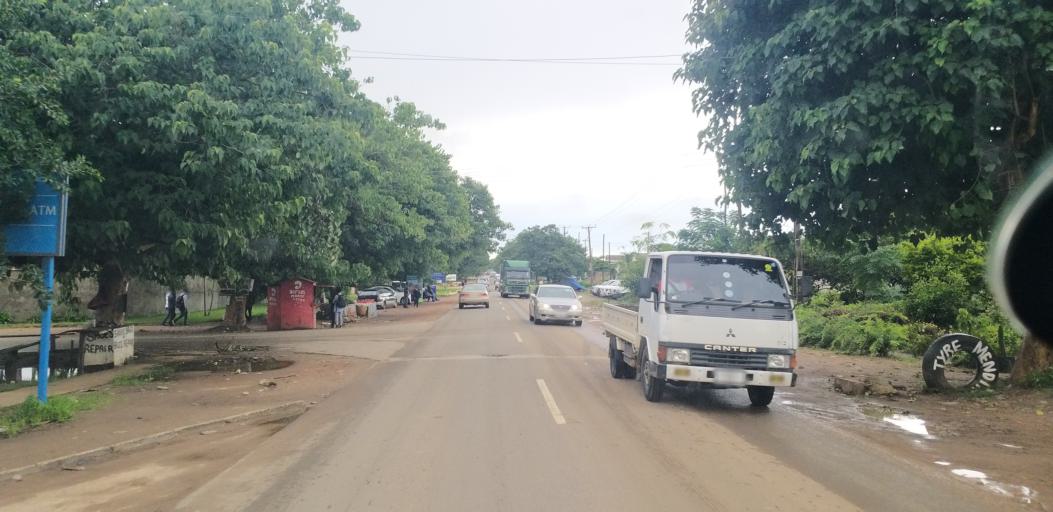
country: ZM
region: Lusaka
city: Lusaka
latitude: -15.4365
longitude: 28.3550
